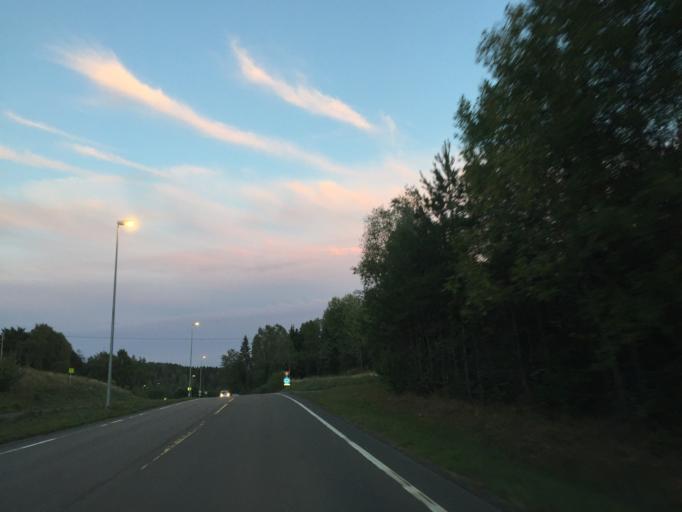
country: NO
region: Akershus
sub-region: Vestby
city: Vestby
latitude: 59.5181
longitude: 10.7181
